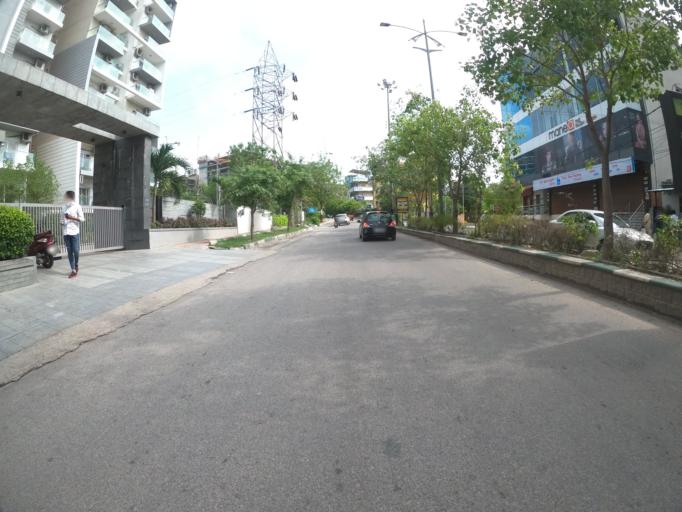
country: IN
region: Telangana
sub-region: Rangareddi
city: Kukatpalli
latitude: 17.4143
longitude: 78.3678
